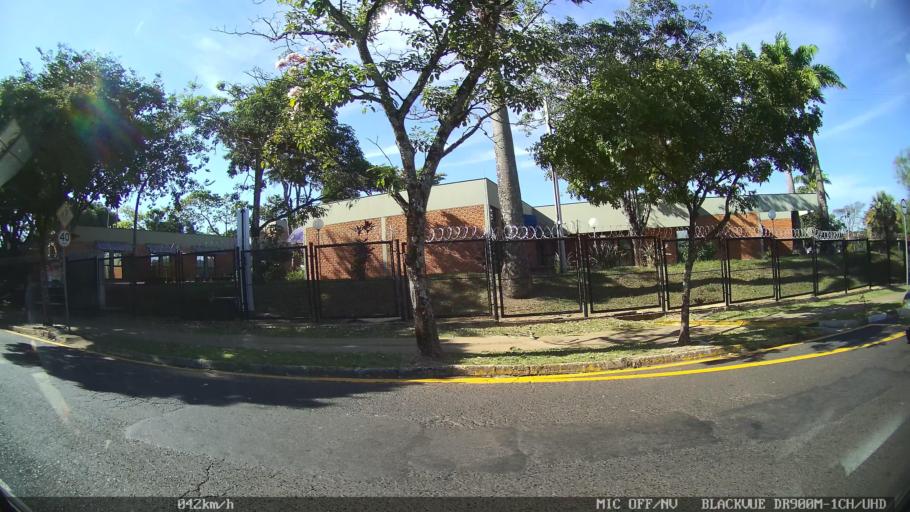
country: BR
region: Sao Paulo
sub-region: Franca
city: Franca
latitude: -20.5085
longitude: -47.4013
